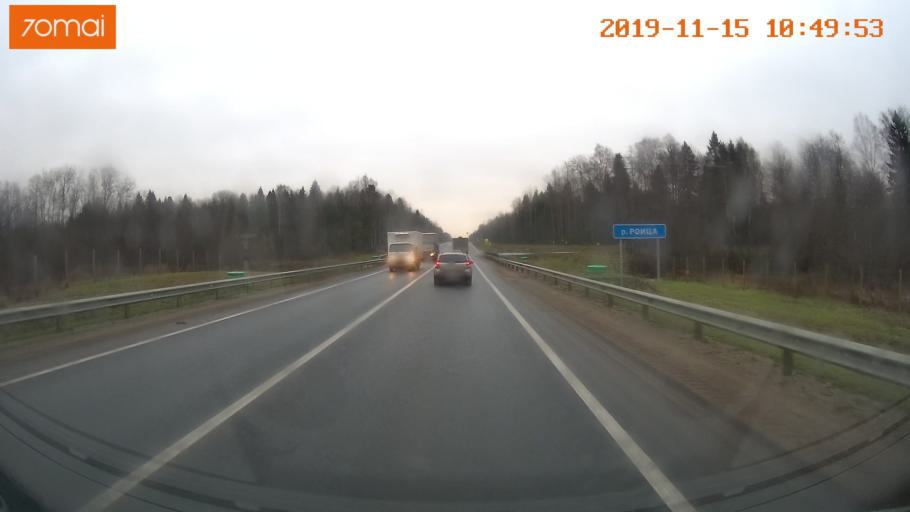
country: RU
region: Vologda
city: Sheksna
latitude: 59.1879
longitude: 38.6697
